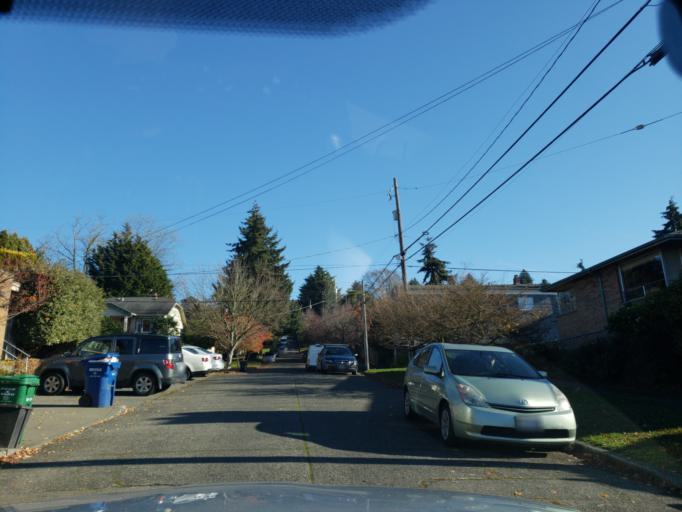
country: US
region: Washington
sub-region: King County
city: Seattle
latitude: 47.6724
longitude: -122.3635
